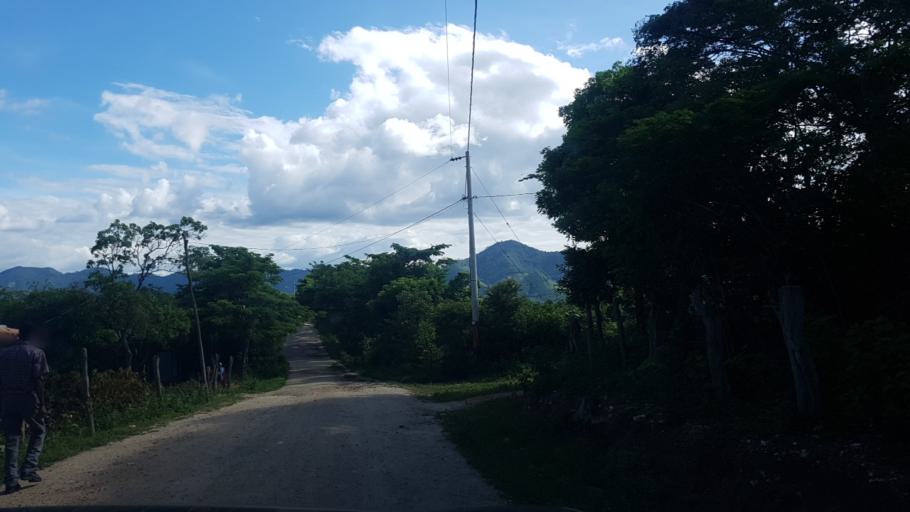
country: NI
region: Nueva Segovia
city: Mozonte
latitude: 13.6470
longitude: -86.3985
